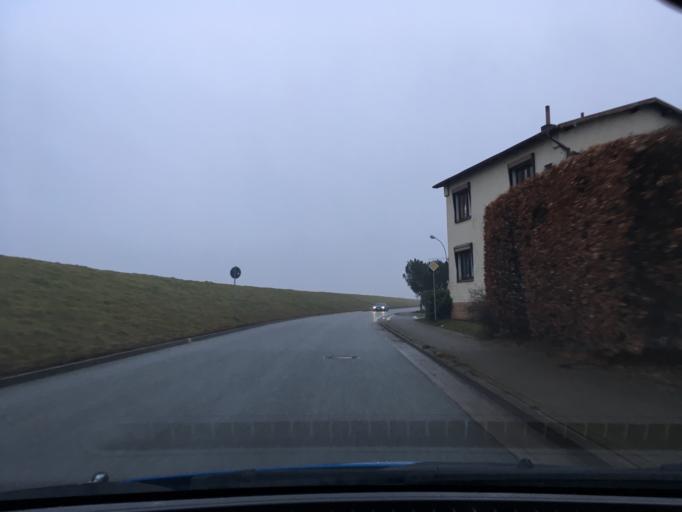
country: DE
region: Lower Saxony
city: Stelle
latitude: 53.4374
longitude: 10.0950
